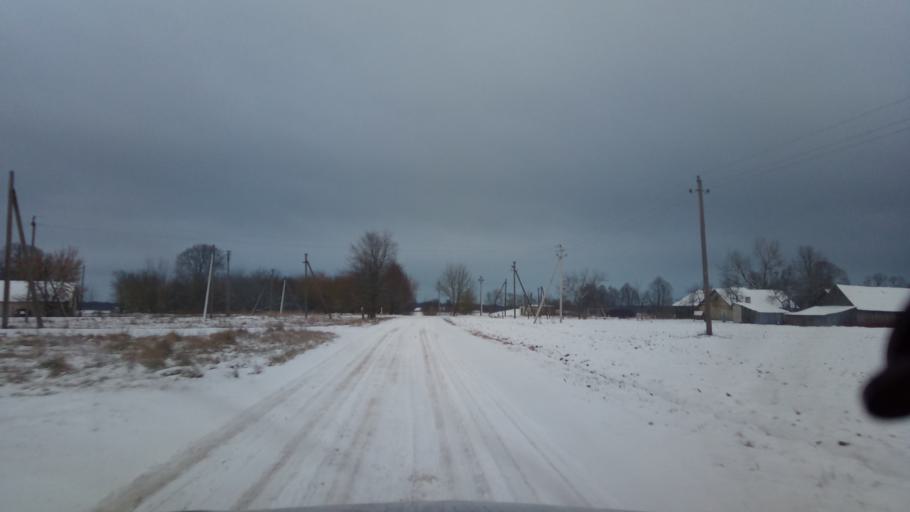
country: LT
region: Vilnius County
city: Ukmerge
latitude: 55.4799
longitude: 24.6169
